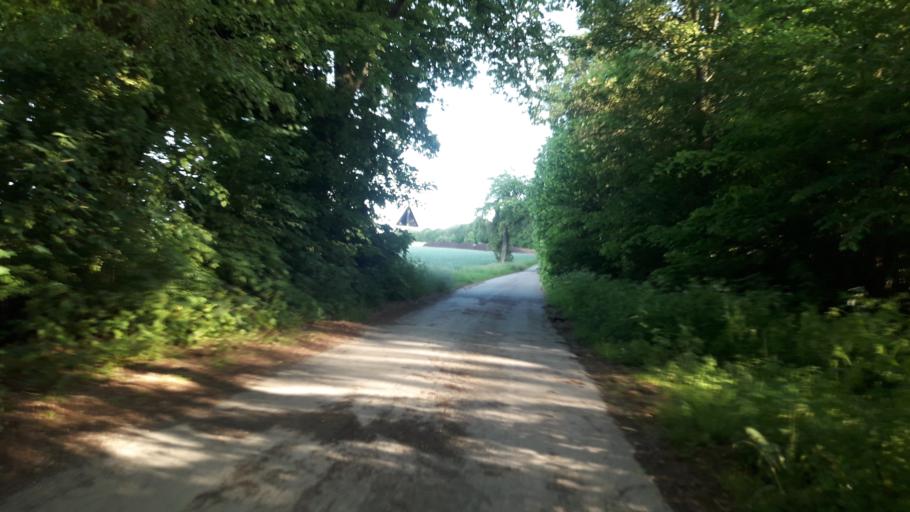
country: DE
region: North Rhine-Westphalia
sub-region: Regierungsbezirk Detmold
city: Paderborn
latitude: 51.6705
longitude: 8.7852
